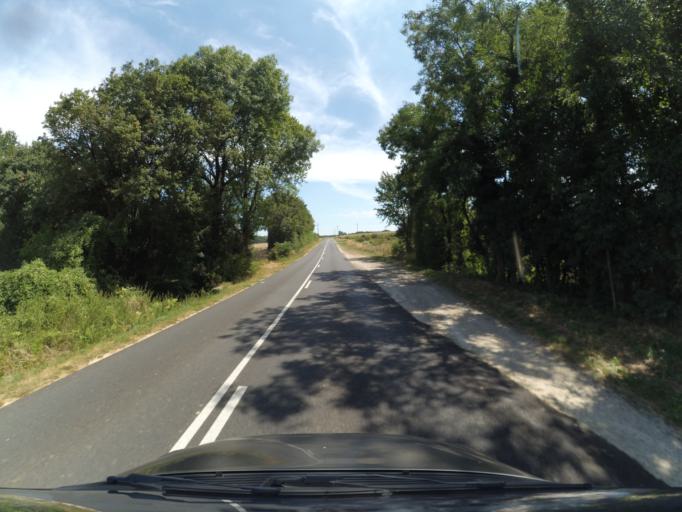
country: FR
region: Poitou-Charentes
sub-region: Departement de la Vienne
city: Saint-Maurice-la-Clouere
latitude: 46.3590
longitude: 0.4376
